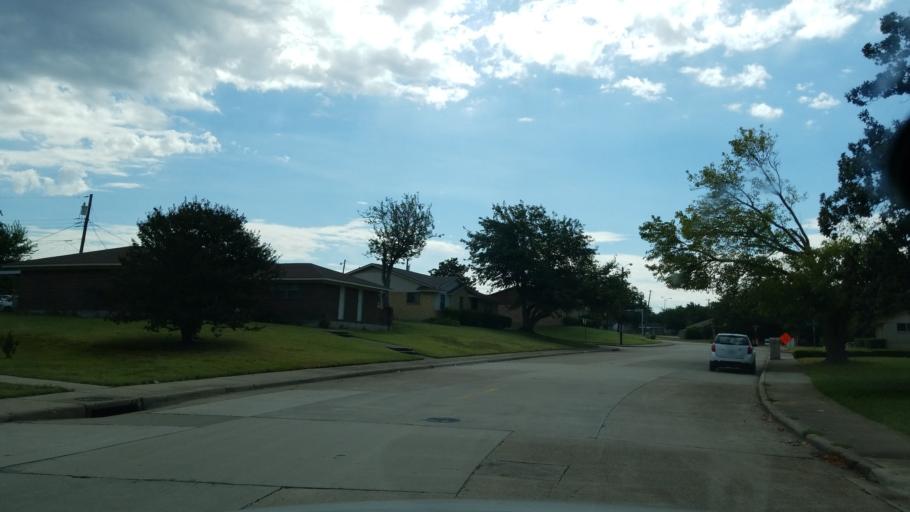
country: US
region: Texas
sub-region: Dallas County
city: DeSoto
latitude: 32.6545
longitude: -96.8418
